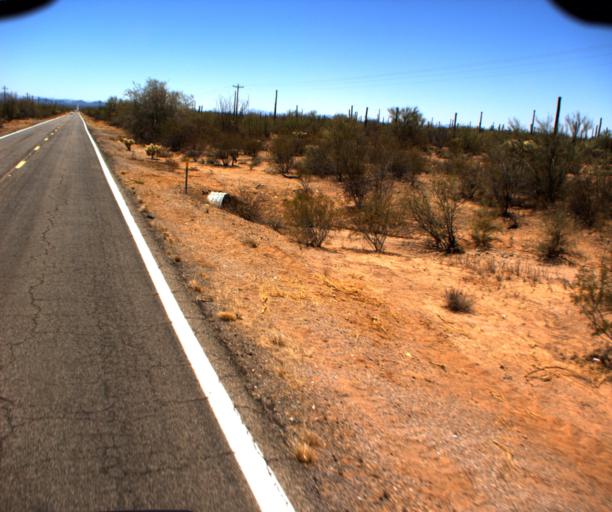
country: US
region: Arizona
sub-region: Pima County
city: Sells
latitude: 32.1318
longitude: -112.0910
